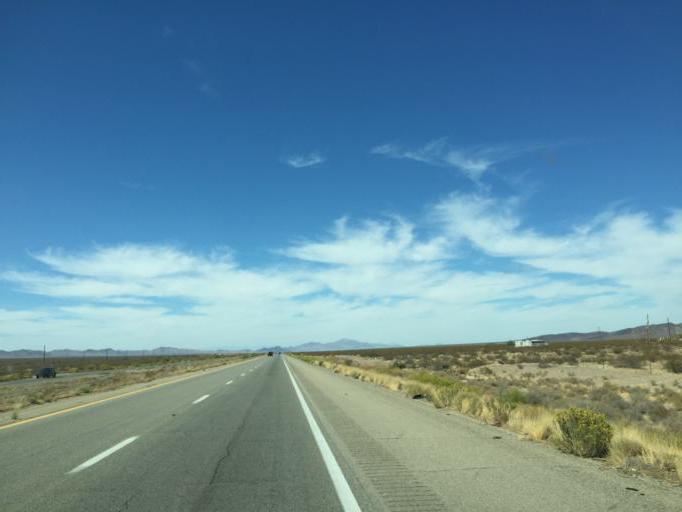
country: US
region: Arizona
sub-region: Mohave County
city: Dolan Springs
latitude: 35.5929
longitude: -114.3960
